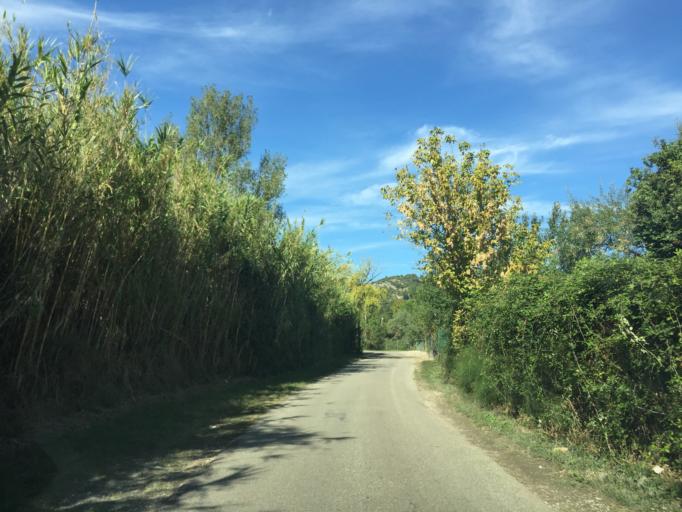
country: FR
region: Provence-Alpes-Cote d'Azur
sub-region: Departement du Vaucluse
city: Mornas
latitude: 44.1958
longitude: 4.7297
